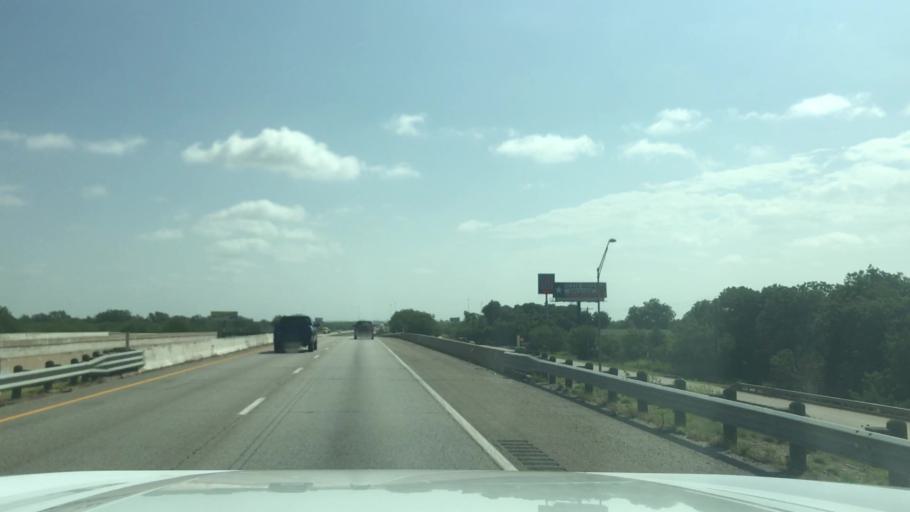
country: US
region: Texas
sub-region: Taylor County
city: Abilene
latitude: 32.4774
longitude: -99.7875
